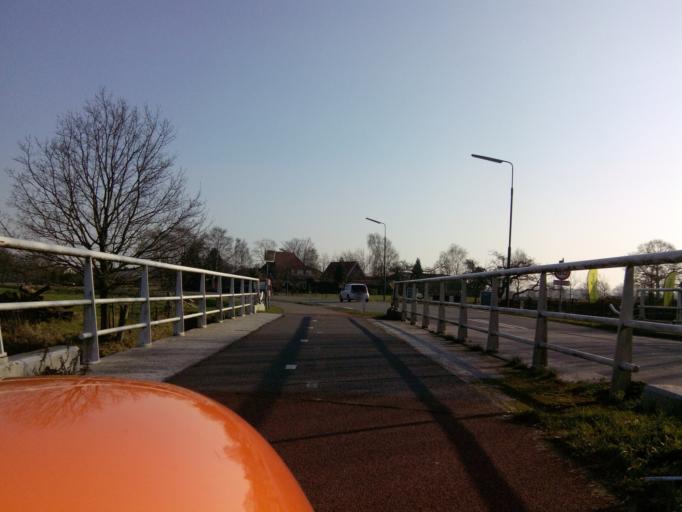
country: NL
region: Utrecht
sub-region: Gemeente Leusden
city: Leusden
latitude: 52.1583
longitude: 5.4265
